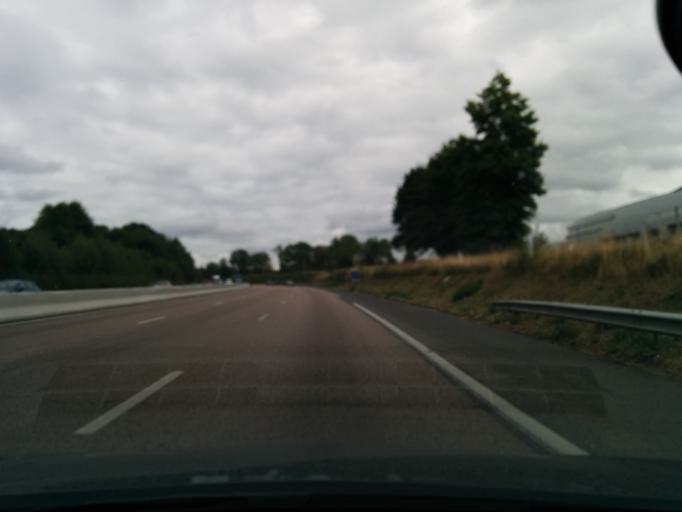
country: FR
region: Limousin
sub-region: Departement de la Haute-Vienne
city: Limoges
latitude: 45.8563
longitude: 1.2807
